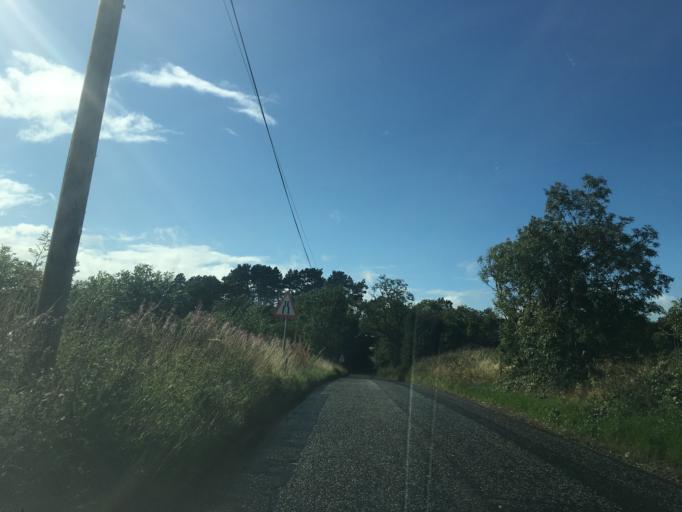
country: GB
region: Scotland
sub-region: Edinburgh
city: Kirkliston
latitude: 55.9663
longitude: -3.3736
